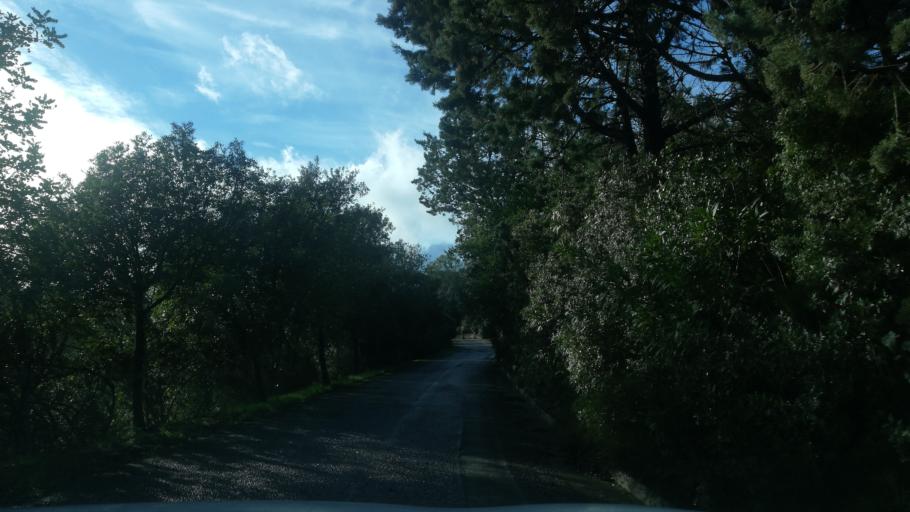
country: IT
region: Sardinia
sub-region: Provincia di Medio Campidano
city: Villanovaforru
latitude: 39.6338
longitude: 8.8569
